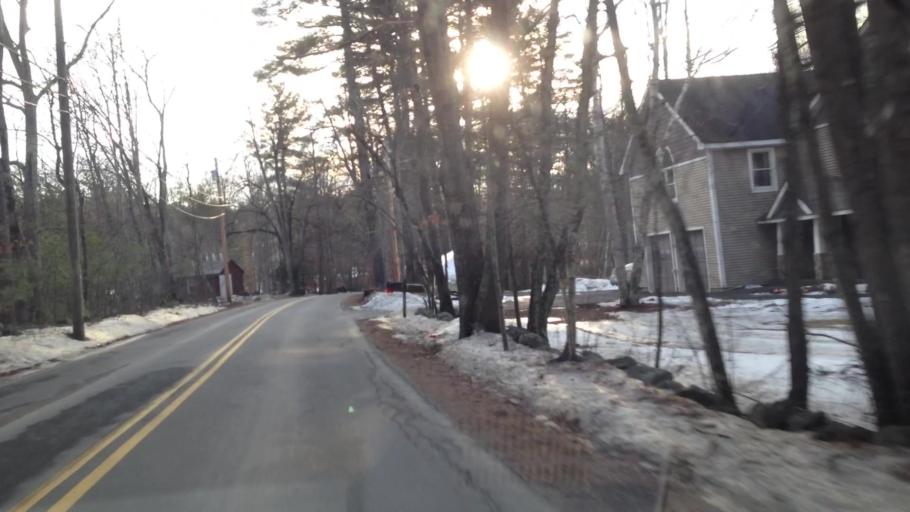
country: US
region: New Hampshire
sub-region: Hillsborough County
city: Merrimack
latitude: 42.8340
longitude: -71.5618
